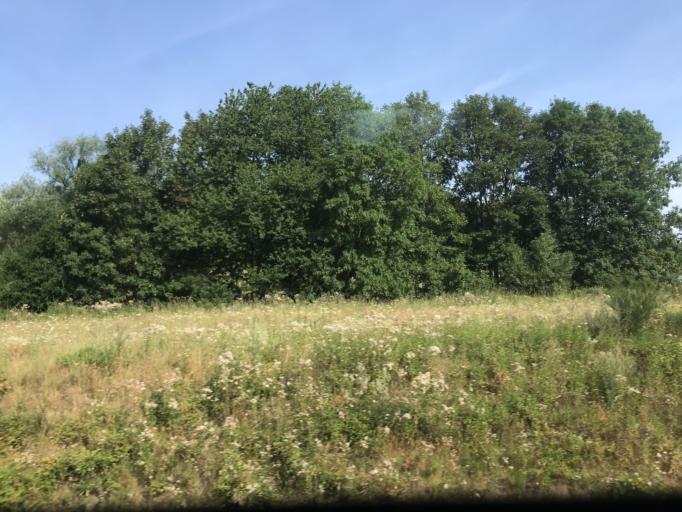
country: CZ
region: Central Bohemia
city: Votice
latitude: 49.6313
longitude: 14.6114
